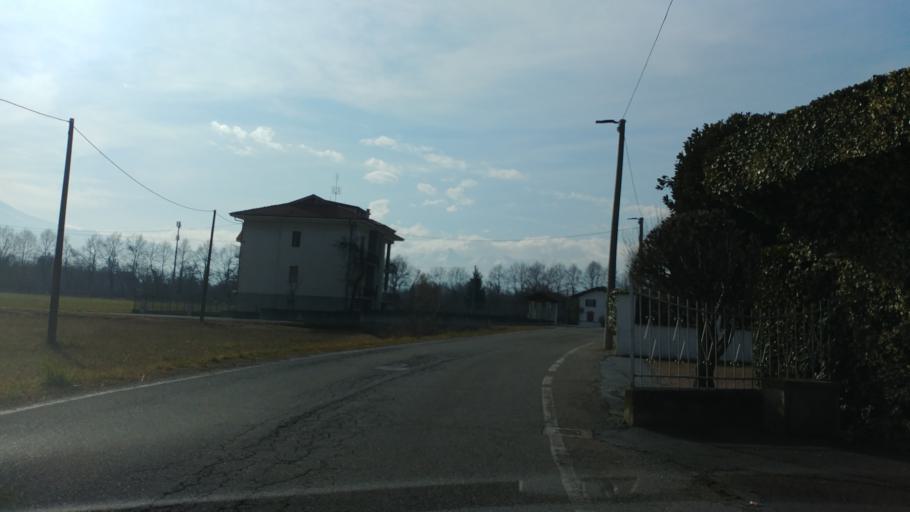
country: IT
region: Piedmont
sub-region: Provincia di Cuneo
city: Cuneo
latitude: 44.3967
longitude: 7.5734
